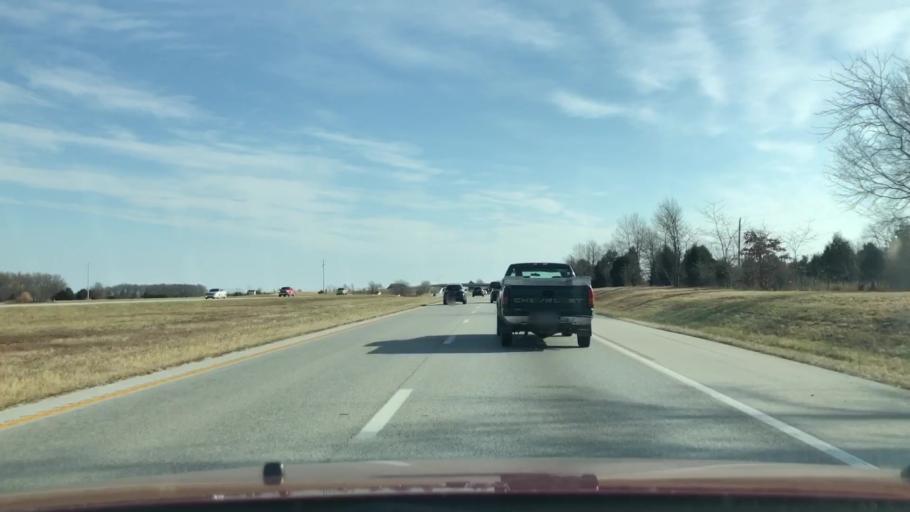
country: US
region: Missouri
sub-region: Webster County
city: Rogersville
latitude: 37.1180
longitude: -93.0949
